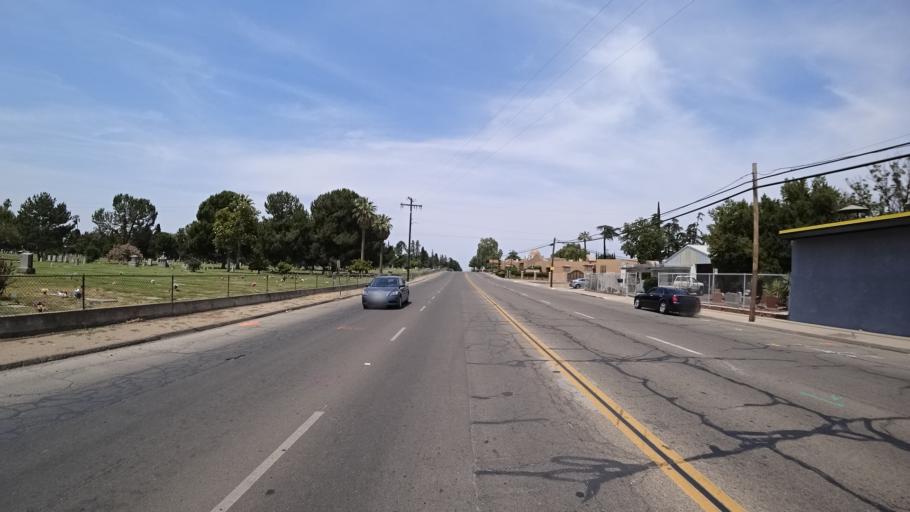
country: US
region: California
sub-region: Fresno County
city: West Park
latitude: 36.7502
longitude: -119.8283
